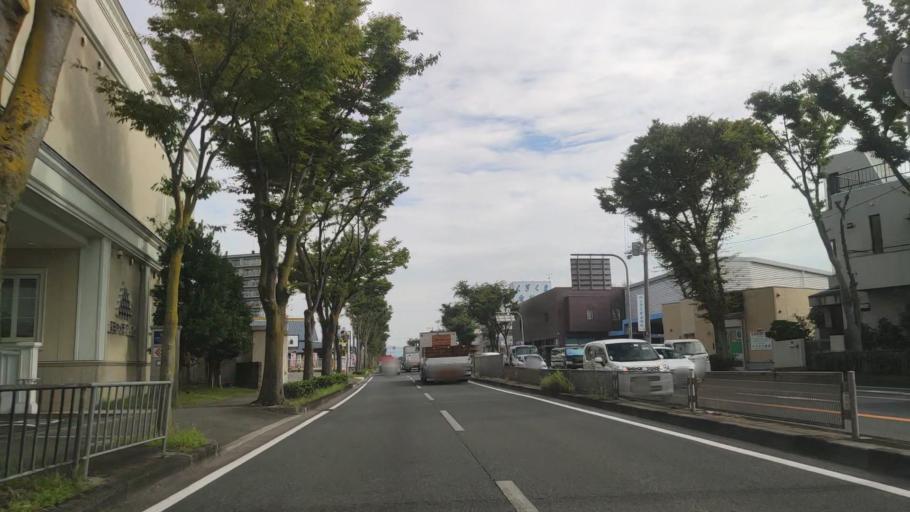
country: JP
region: Osaka
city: Tondabayashicho
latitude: 34.5088
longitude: 135.6010
